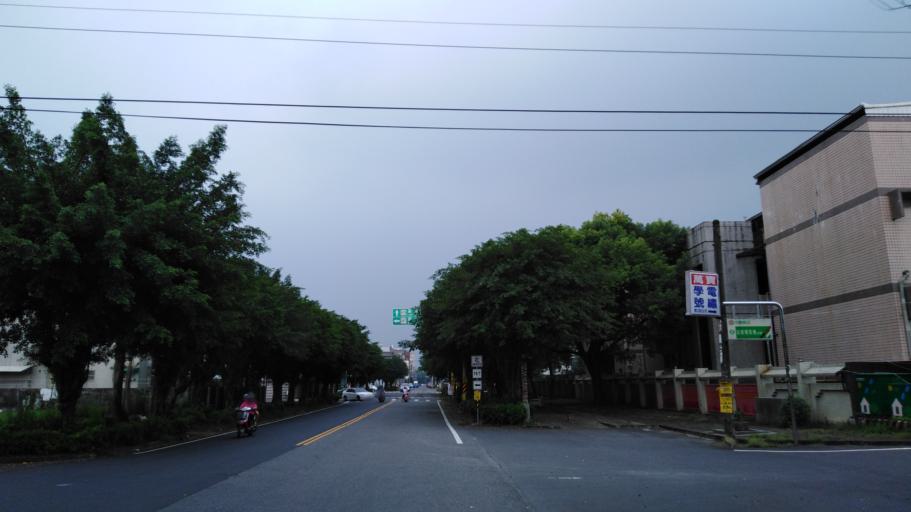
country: TW
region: Taiwan
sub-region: Pingtung
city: Pingtung
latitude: 22.5498
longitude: 120.5441
